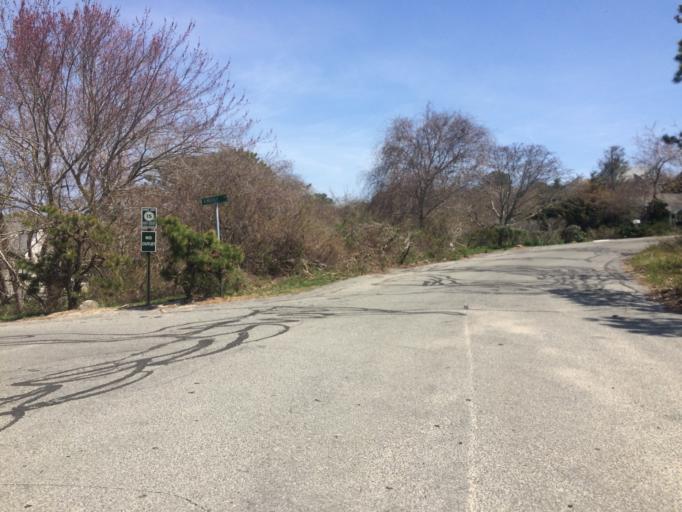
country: US
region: Massachusetts
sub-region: Barnstable County
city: Provincetown
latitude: 42.0460
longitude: -70.1989
